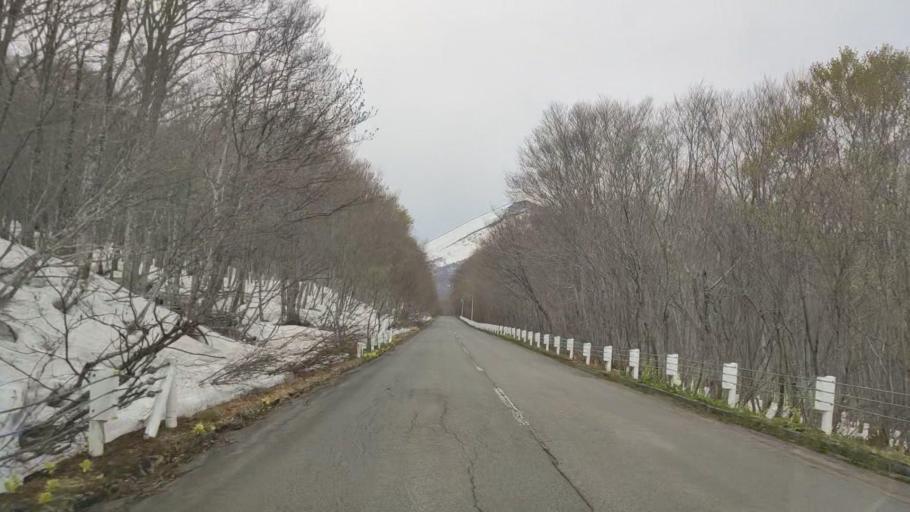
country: JP
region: Aomori
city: Aomori Shi
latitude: 40.6537
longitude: 140.9532
